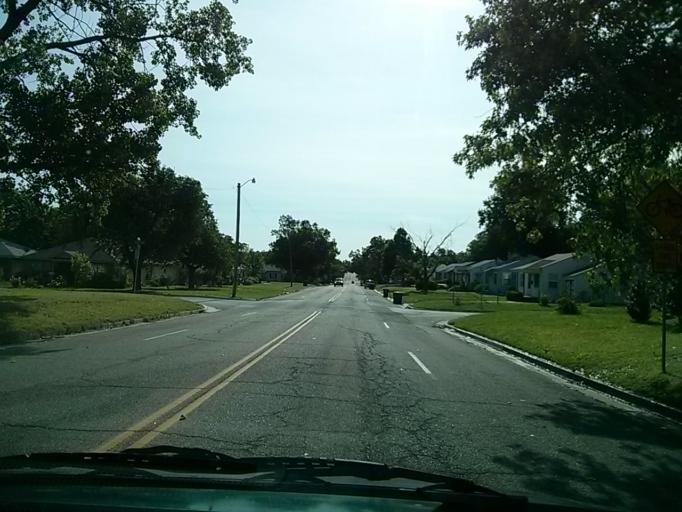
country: US
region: Oklahoma
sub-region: Tulsa County
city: Tulsa
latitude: 36.1552
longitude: -95.9028
